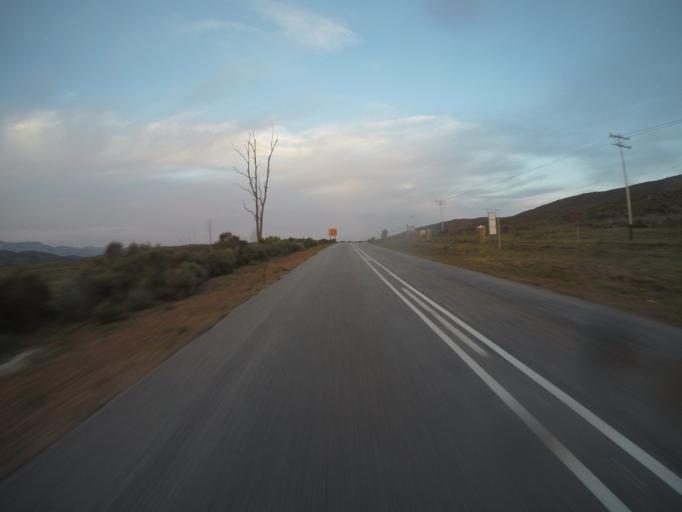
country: ZA
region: Western Cape
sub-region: Eden District Municipality
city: Plettenberg Bay
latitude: -33.7409
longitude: 23.4376
